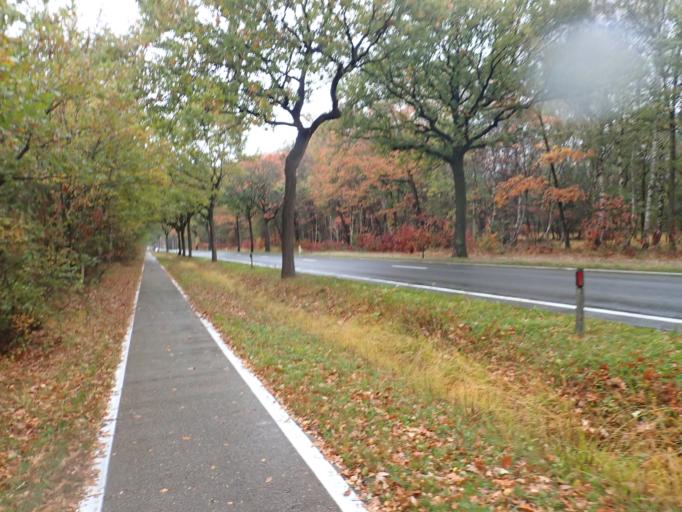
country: BE
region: Flanders
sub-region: Provincie Antwerpen
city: Wuustwezel
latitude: 51.3728
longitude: 4.6112
